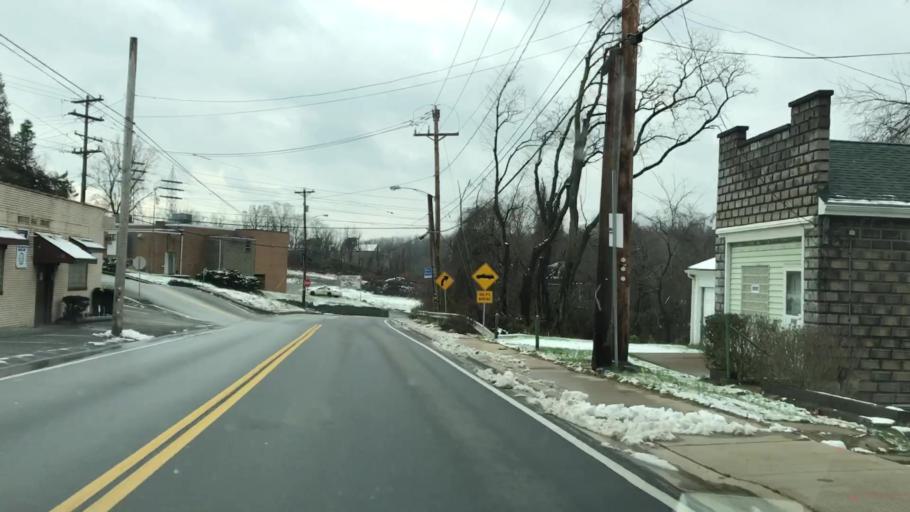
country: US
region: Pennsylvania
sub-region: Allegheny County
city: Monroeville
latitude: 40.4688
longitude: -79.7910
